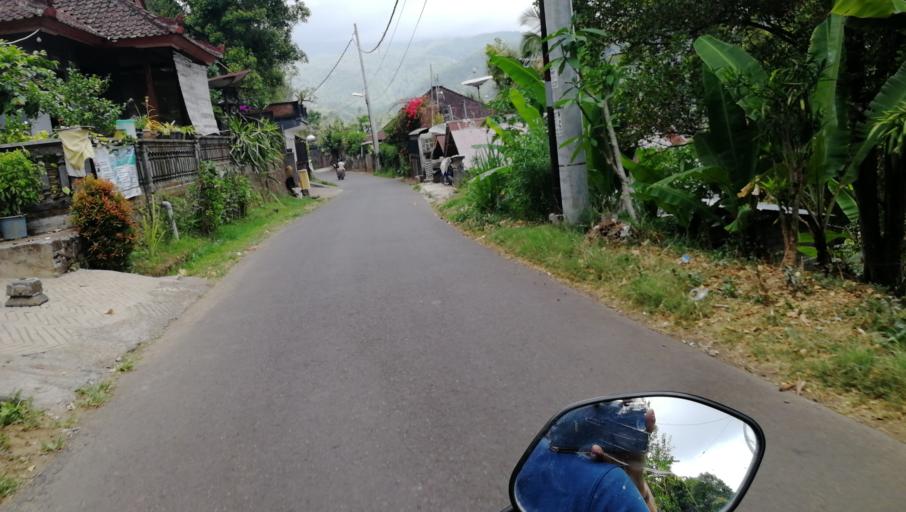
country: ID
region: Bali
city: Banjar Pedawa
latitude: -8.2647
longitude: 115.0424
